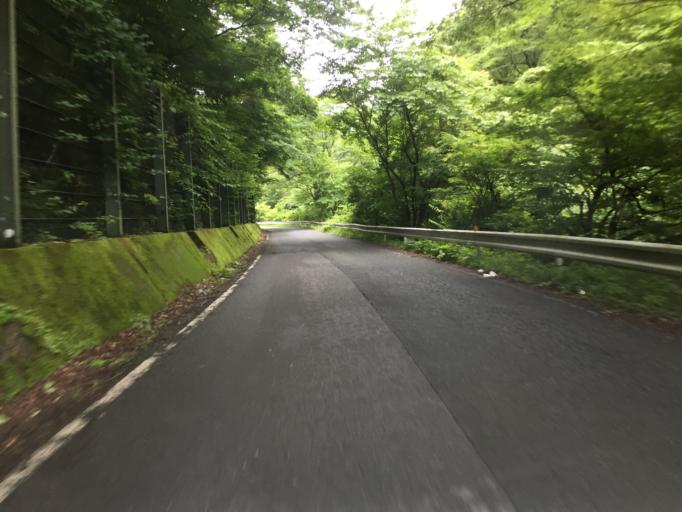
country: JP
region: Fukushima
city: Namie
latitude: 37.6806
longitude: 140.8625
